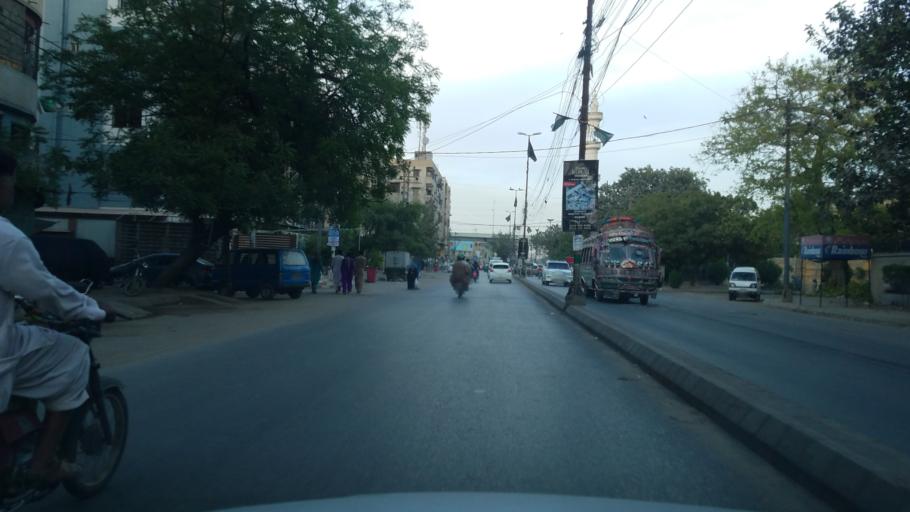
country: PK
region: Sindh
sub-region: Karachi District
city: Karachi
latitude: 24.8787
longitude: 67.0372
